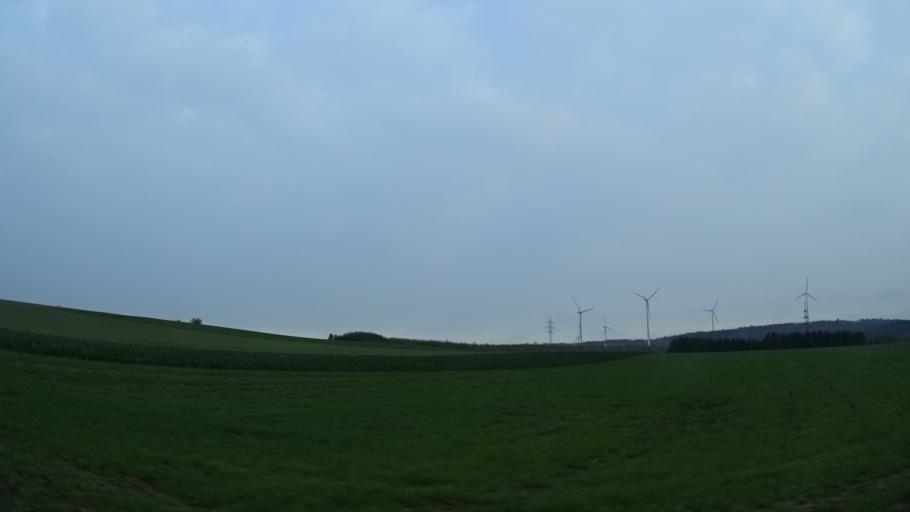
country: DE
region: Rheinland-Pfalz
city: Hoppstadten-Weiersbach
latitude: 49.6276
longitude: 7.2157
